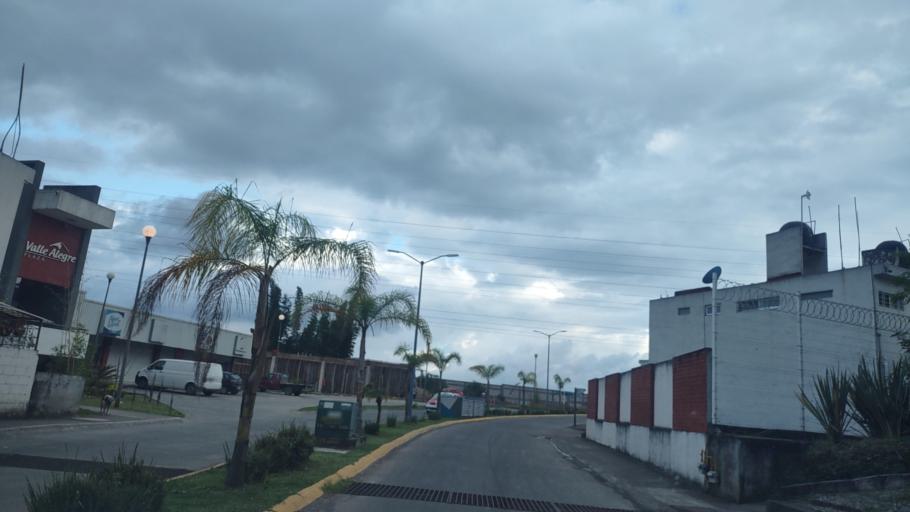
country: MX
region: Veracruz
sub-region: Ixtaczoquitlan
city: Buenavista
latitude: 18.8822
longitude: -97.0587
